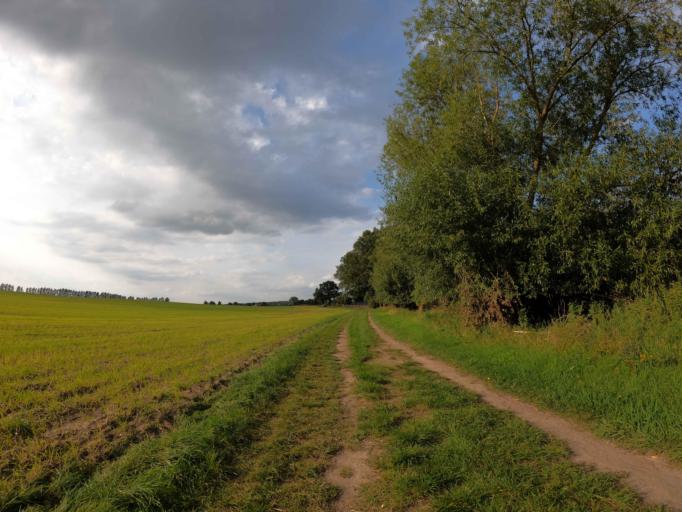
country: DE
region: Mecklenburg-Vorpommern
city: Klink
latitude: 53.4482
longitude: 12.5239
